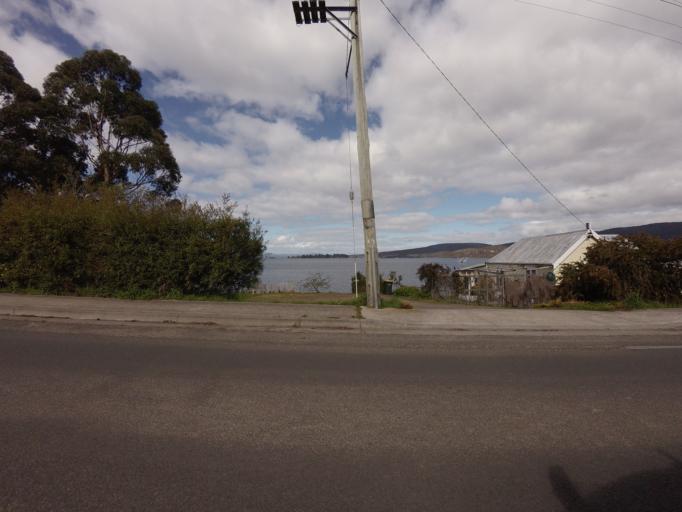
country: AU
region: Tasmania
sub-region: Huon Valley
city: Cygnet
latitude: -43.3180
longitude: 147.0101
